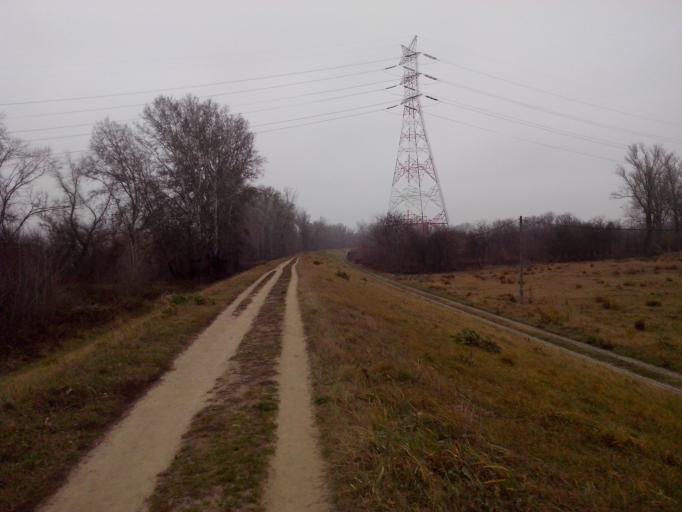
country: PL
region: Masovian Voivodeship
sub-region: Powiat legionowski
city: Jablonna
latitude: 52.3498
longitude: 20.9225
